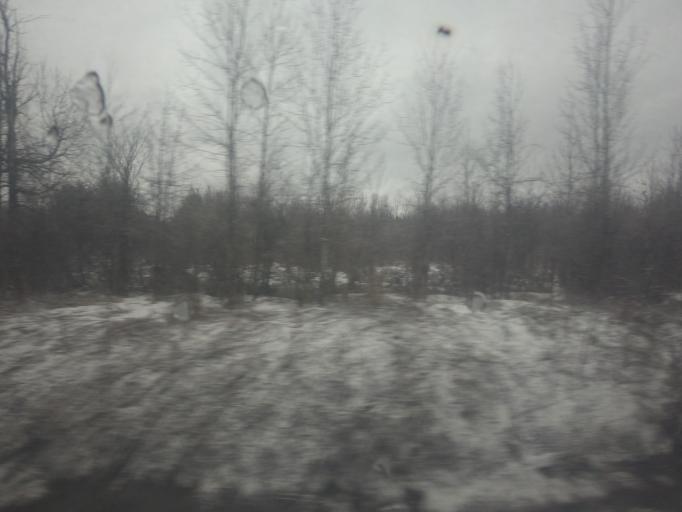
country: CA
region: Ontario
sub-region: Lanark County
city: Smiths Falls
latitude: 44.9352
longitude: -76.0259
